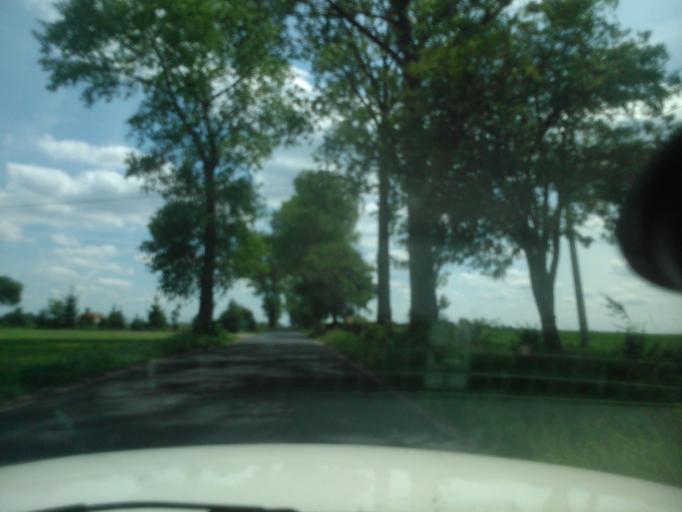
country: PL
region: Kujawsko-Pomorskie
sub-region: Powiat torunski
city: Obrowo
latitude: 53.0253
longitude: 18.8511
